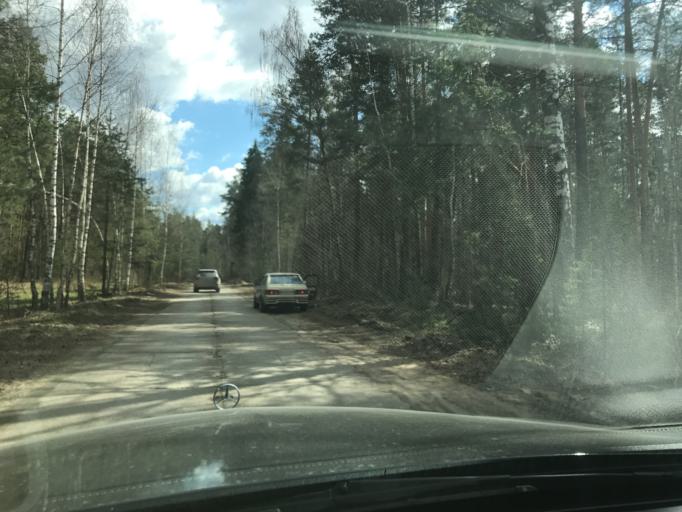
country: RU
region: Moskovskaya
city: Vereya
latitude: 55.8407
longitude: 39.1045
